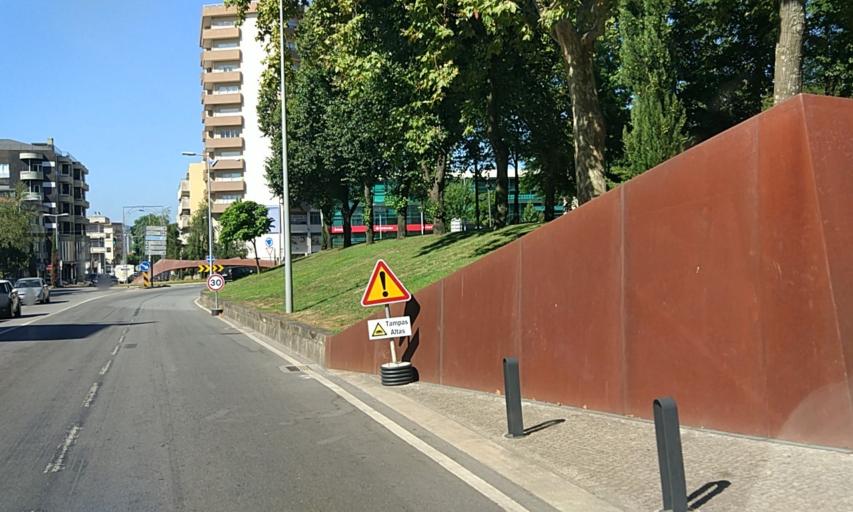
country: PT
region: Porto
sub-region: Trofa
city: Bougado
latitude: 41.3345
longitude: -8.5603
